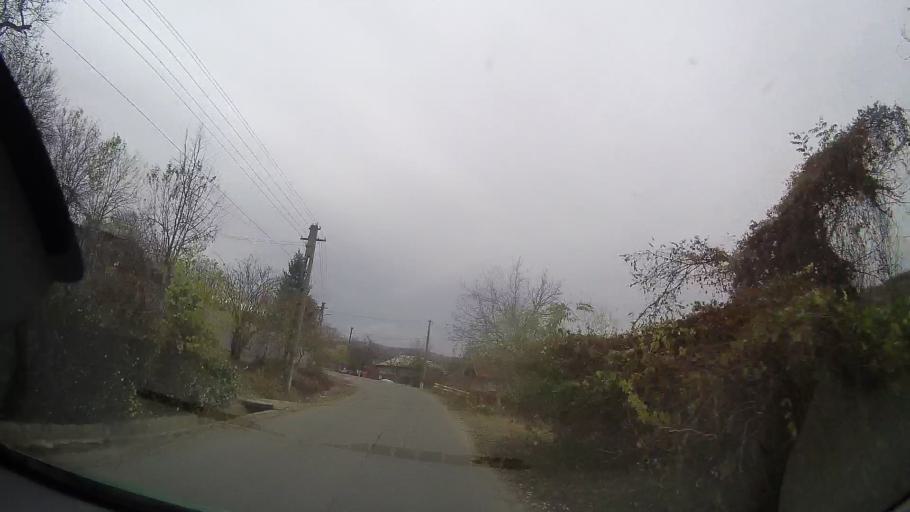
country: RO
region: Prahova
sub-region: Comuna Gornet-Cricov
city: Gornet-Cricov
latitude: 45.0581
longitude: 26.2811
